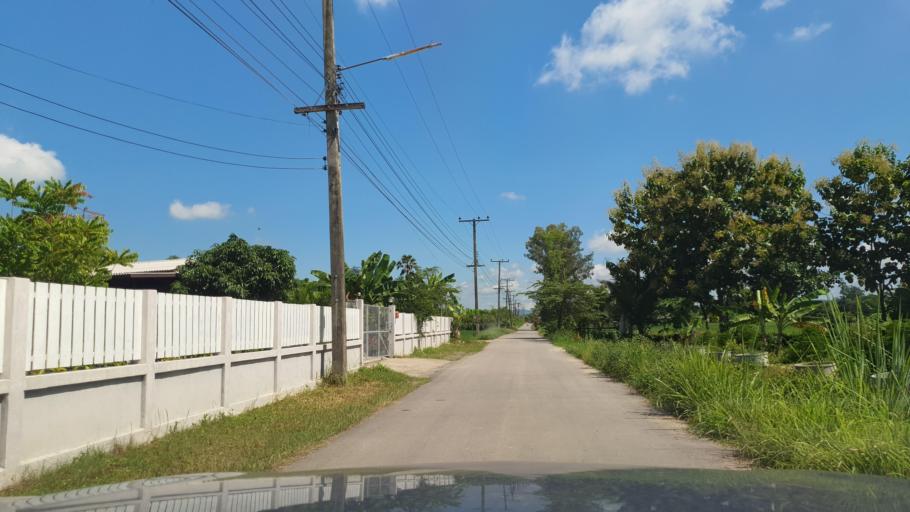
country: TH
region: Chiang Mai
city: San Kamphaeng
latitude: 18.7705
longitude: 99.1691
